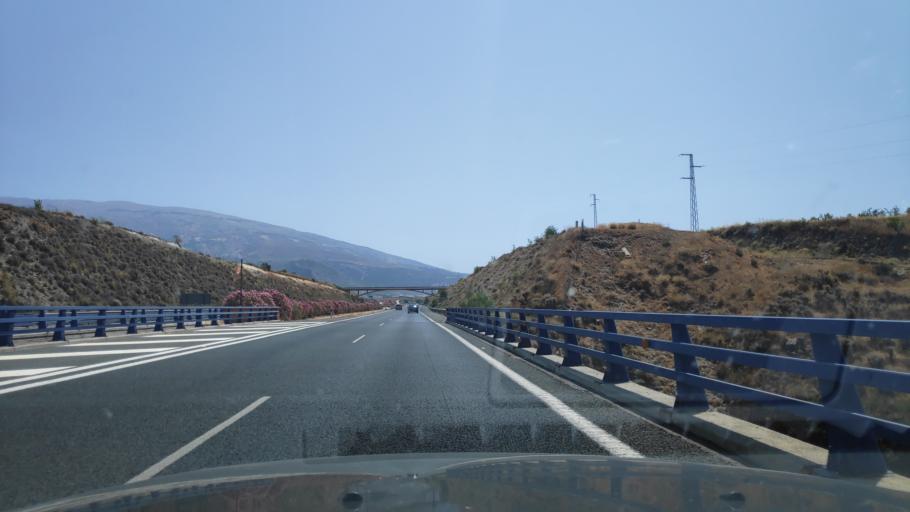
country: ES
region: Andalusia
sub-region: Provincia de Granada
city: Durcal
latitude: 36.9841
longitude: -3.5837
